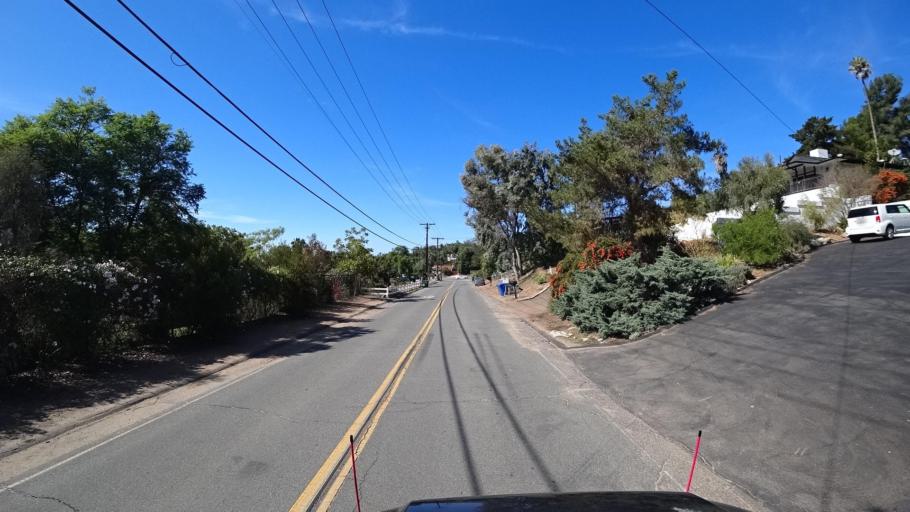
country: US
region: California
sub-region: San Diego County
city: Casa de Oro-Mount Helix
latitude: 32.7579
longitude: -116.9603
